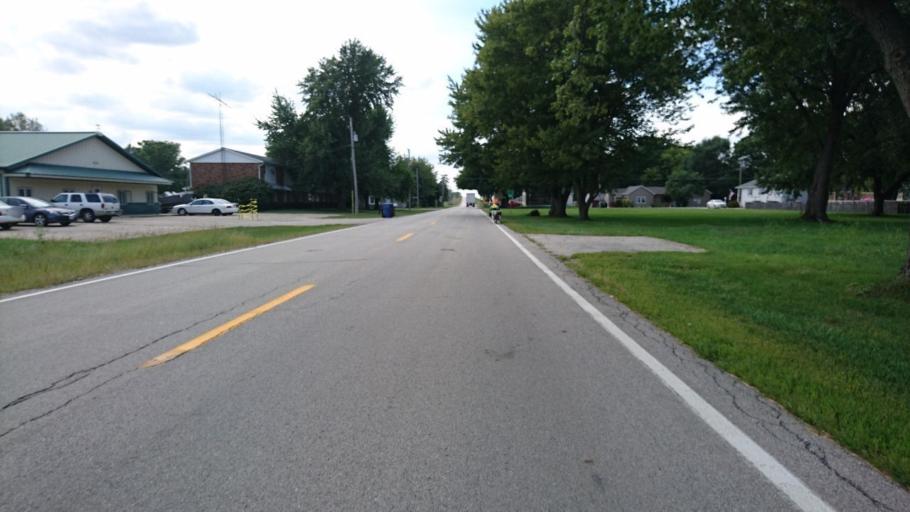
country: US
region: Illinois
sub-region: Grundy County
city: Gardner
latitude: 41.1824
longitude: -88.3069
